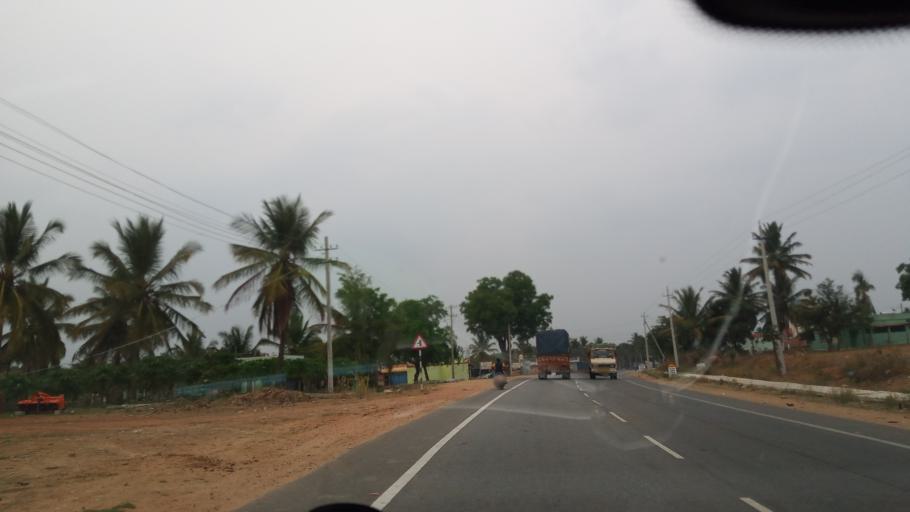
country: IN
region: Karnataka
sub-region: Mandya
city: Nagamangala
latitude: 12.8061
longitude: 76.7528
